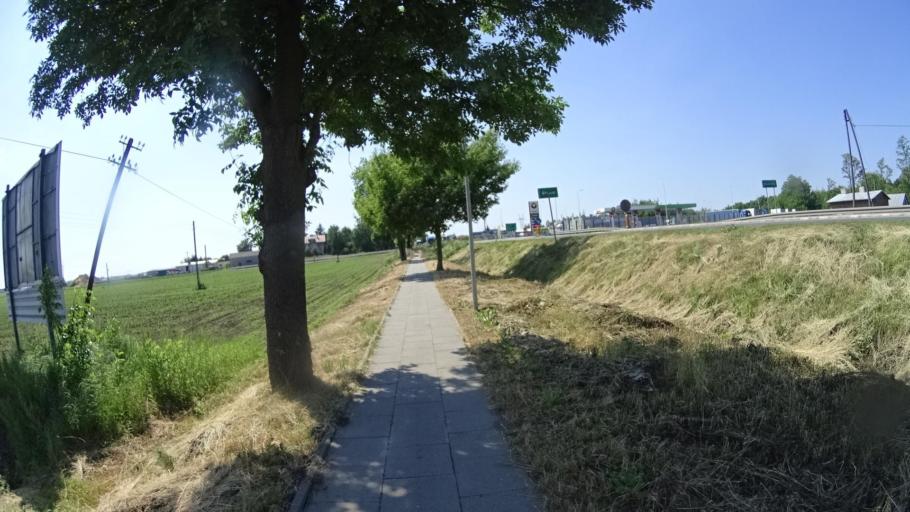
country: PL
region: Masovian Voivodeship
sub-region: Powiat warszawski zachodni
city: Blonie
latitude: 52.1991
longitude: 20.6024
